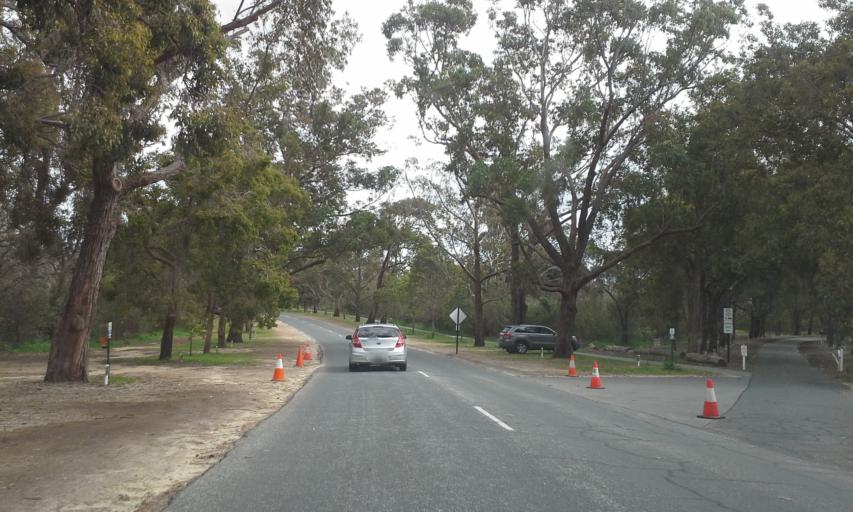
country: AU
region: Western Australia
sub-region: City of Perth
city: West Perth
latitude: -31.9581
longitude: 115.8390
